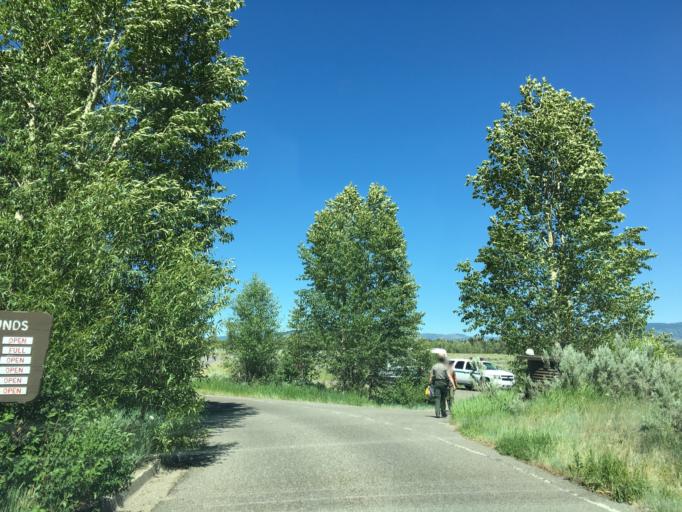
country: US
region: Wyoming
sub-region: Teton County
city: Moose Wilson Road
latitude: 43.5970
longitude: -110.8036
